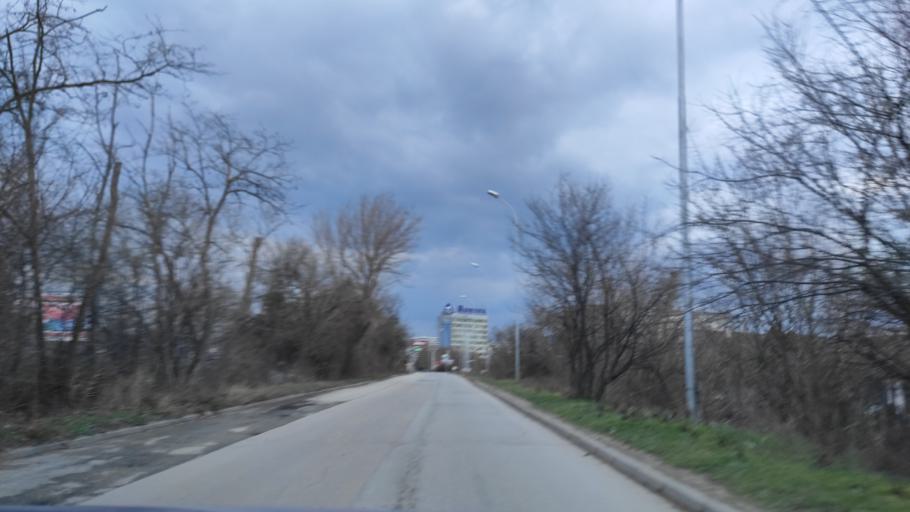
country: BG
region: Varna
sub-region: Obshtina Varna
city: Varna
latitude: 43.2234
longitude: 27.8667
